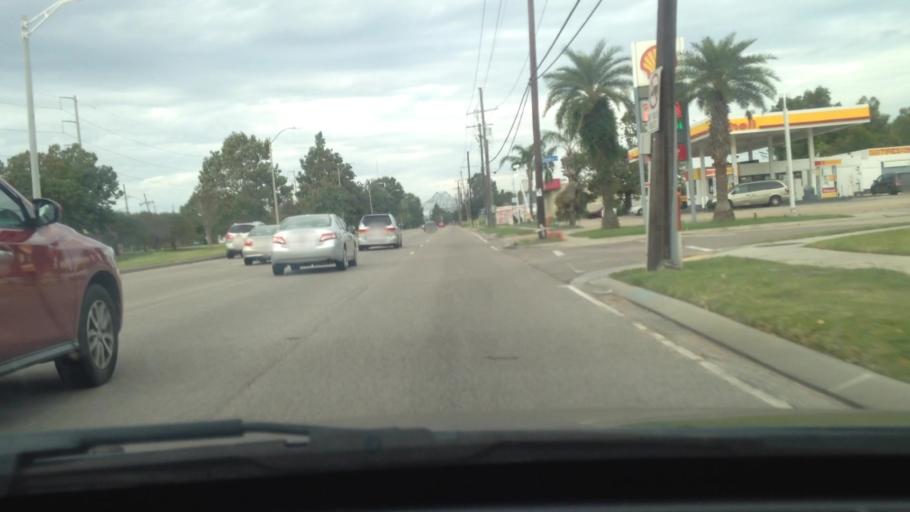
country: US
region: Louisiana
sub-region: Jefferson Parish
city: Terrytown
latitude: 29.9264
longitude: -90.0240
